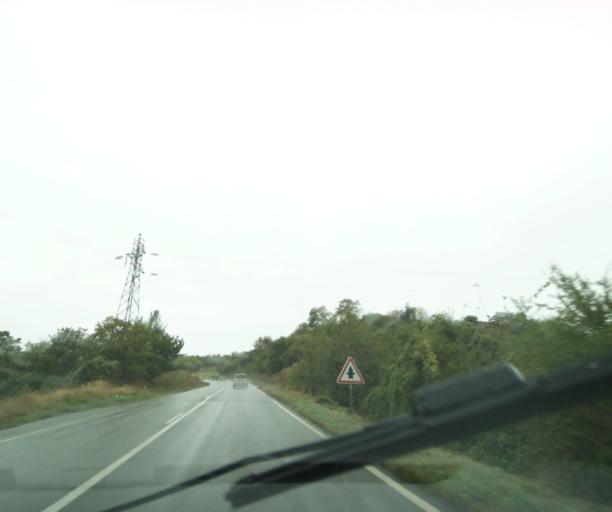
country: FR
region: Auvergne
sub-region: Departement du Puy-de-Dome
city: Cebazat
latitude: 45.8448
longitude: 3.1064
